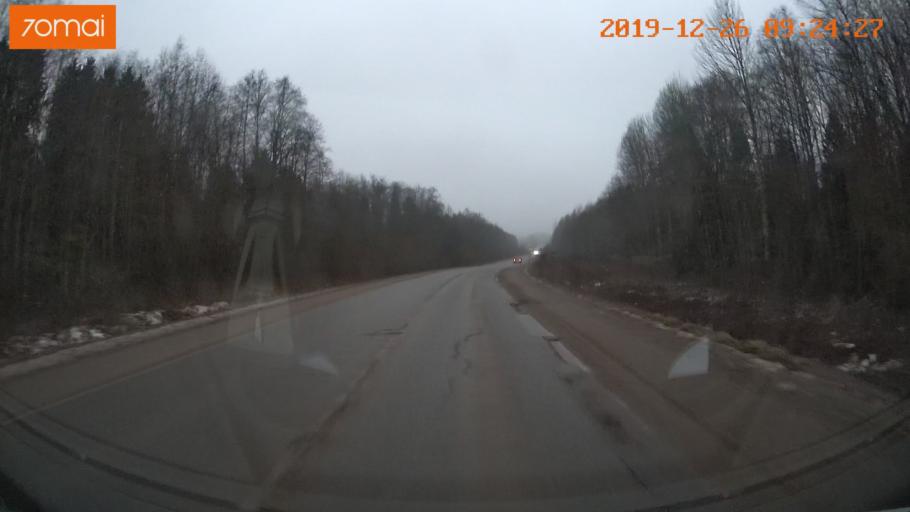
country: RU
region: Vologda
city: Gryazovets
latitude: 59.0008
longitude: 40.1984
